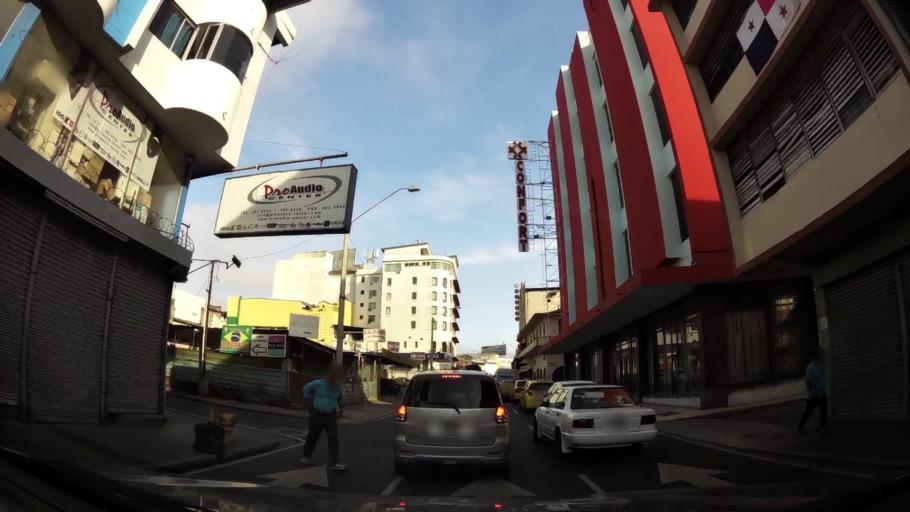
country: PA
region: Panama
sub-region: Distrito de Panama
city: Ancon
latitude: 8.9594
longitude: -79.5403
